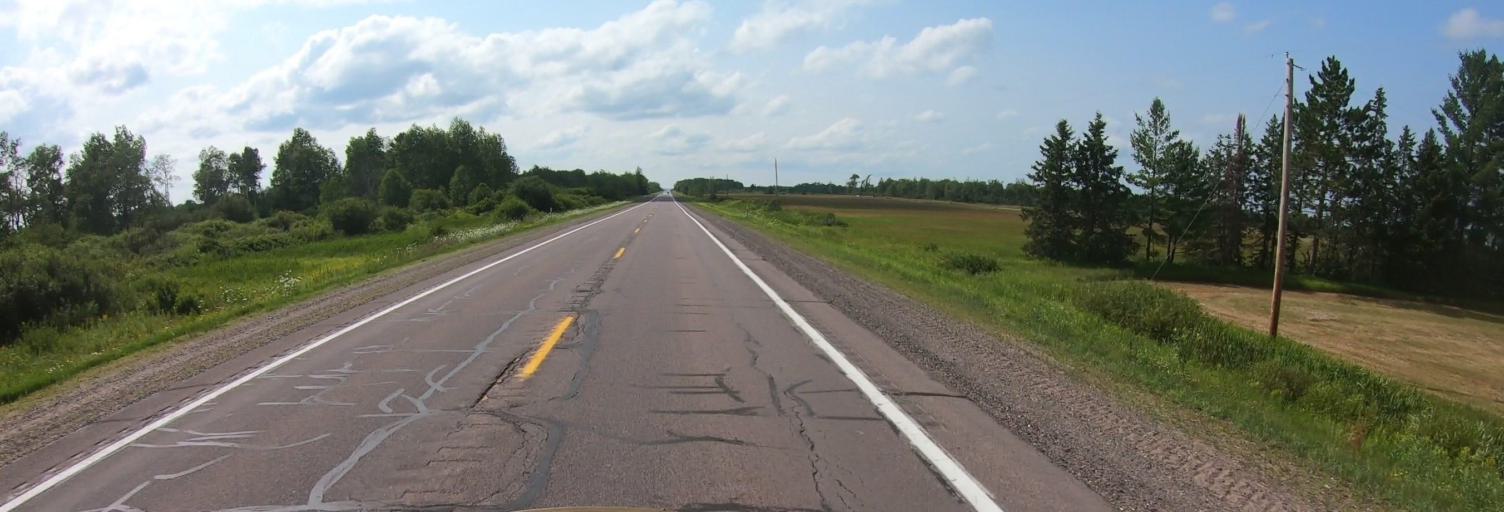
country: US
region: Michigan
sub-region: Ontonagon County
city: Ontonagon
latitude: 46.5498
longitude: -89.3680
